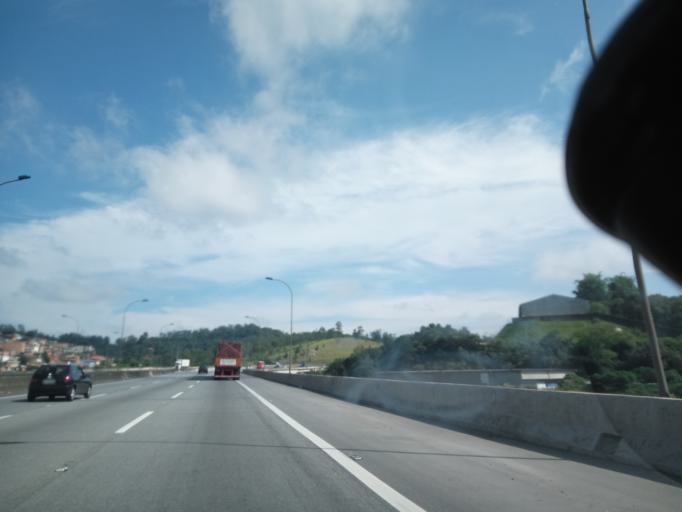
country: BR
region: Sao Paulo
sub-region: Embu
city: Embu
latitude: -23.6414
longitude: -46.8327
